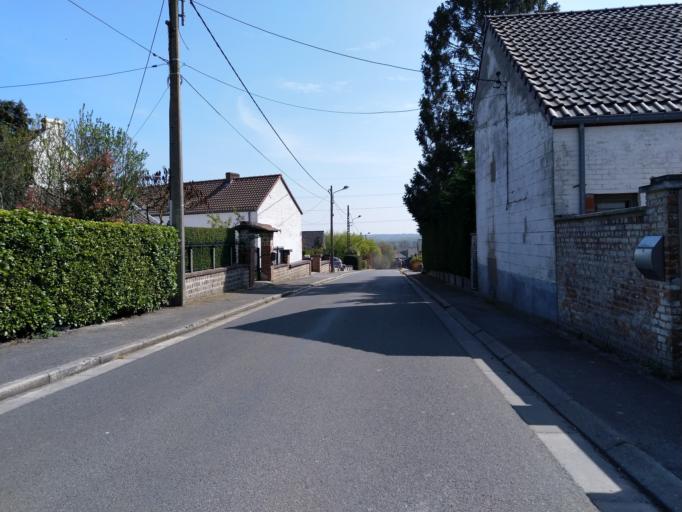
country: BE
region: Wallonia
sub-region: Province du Hainaut
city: Mons
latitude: 50.4818
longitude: 4.0070
